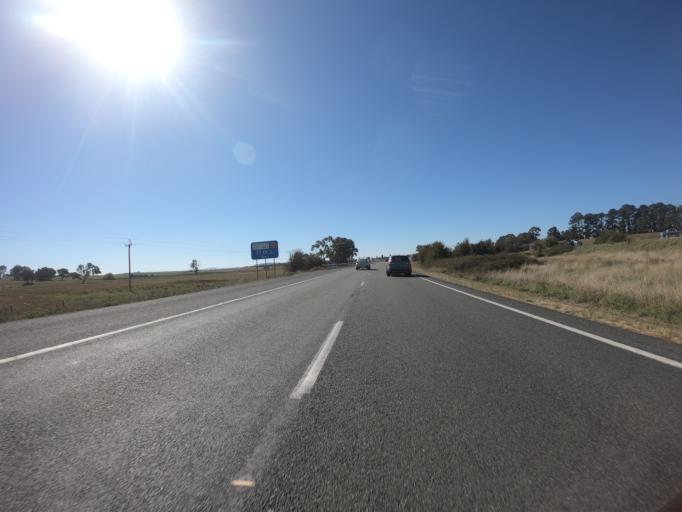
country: AU
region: New South Wales
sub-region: Goulburn Mulwaree
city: Goulburn
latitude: -34.7913
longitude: 149.6197
